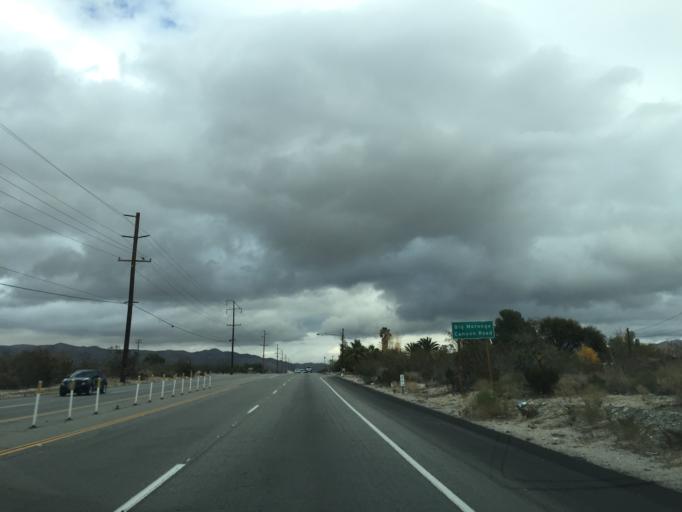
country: US
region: California
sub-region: San Bernardino County
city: Morongo Valley
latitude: 34.0648
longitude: -116.5580
